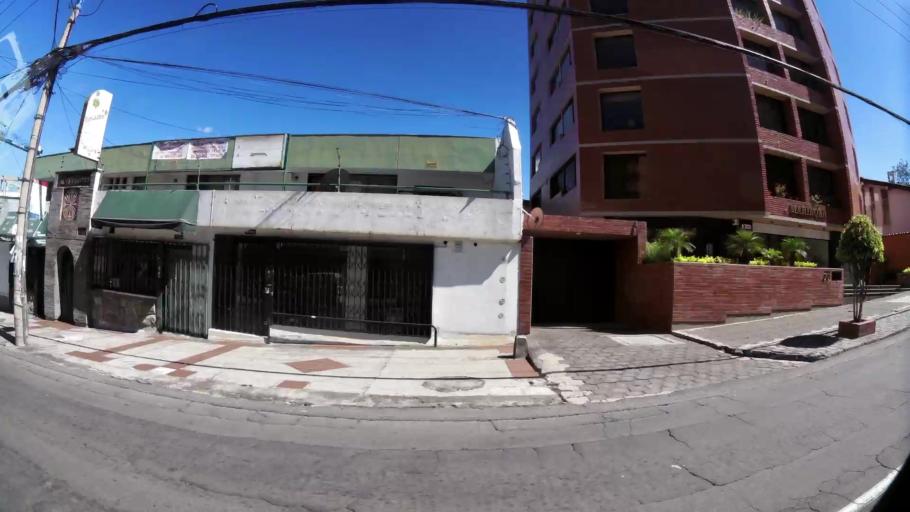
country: EC
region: Pichincha
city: Quito
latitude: -0.1854
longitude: -78.4776
